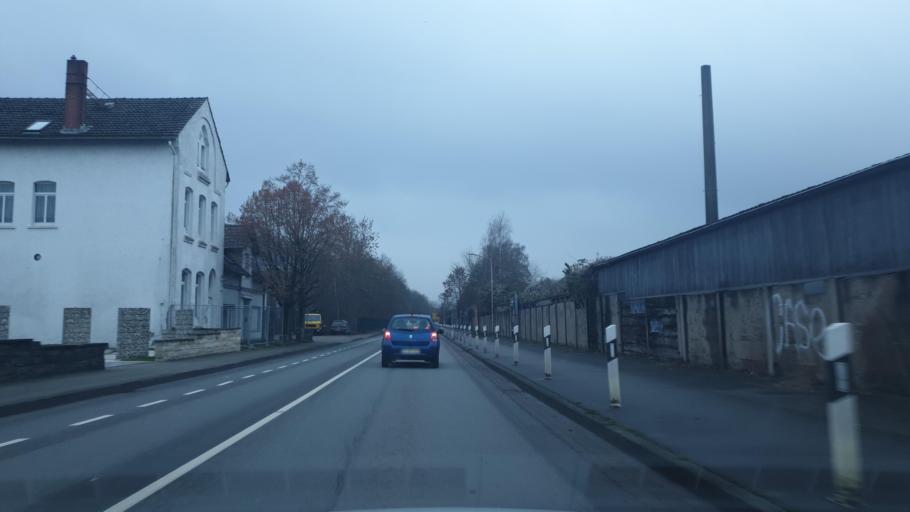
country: DE
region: North Rhine-Westphalia
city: Porta Westfalica
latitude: 52.2545
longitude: 8.9298
